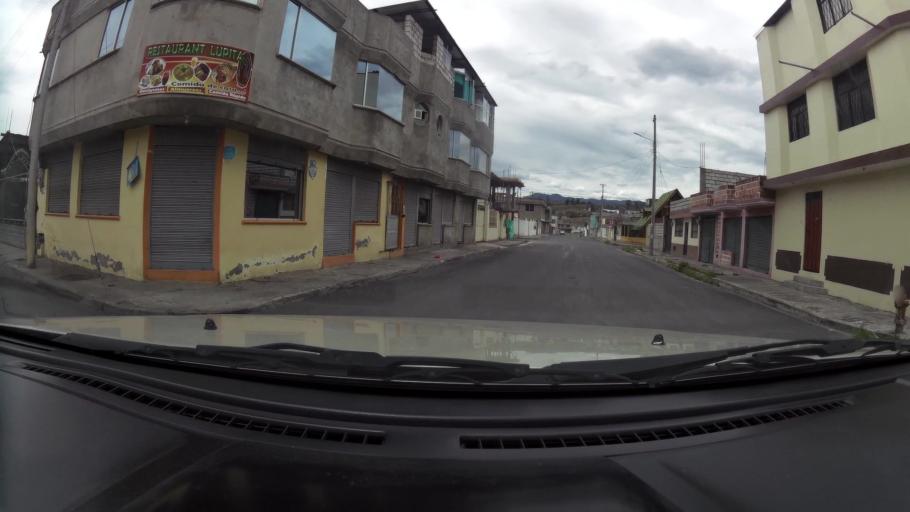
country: EC
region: Cotopaxi
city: Latacunga
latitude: -0.9574
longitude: -78.6055
